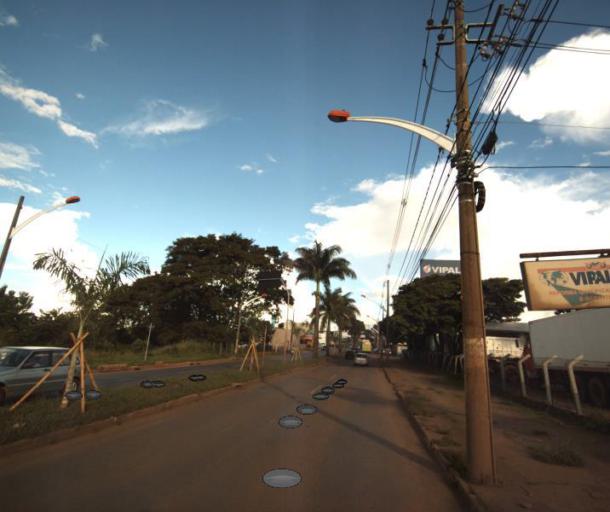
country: BR
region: Goias
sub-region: Anapolis
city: Anapolis
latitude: -16.3517
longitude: -48.9327
